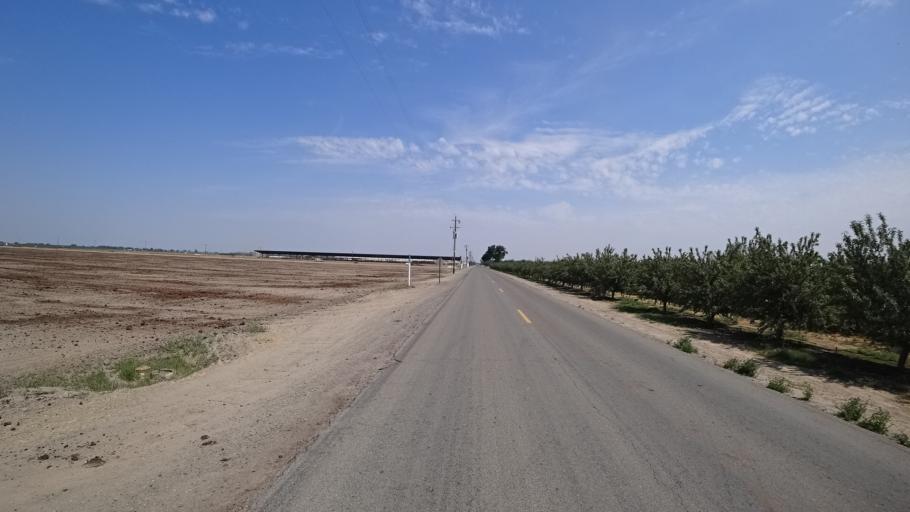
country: US
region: California
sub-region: Kings County
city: Armona
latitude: 36.3728
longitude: -119.7450
